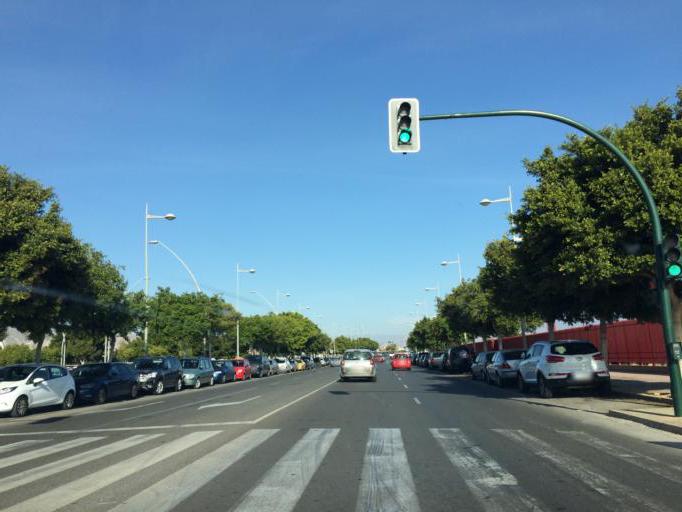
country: ES
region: Andalusia
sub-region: Provincia de Almeria
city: Almeria
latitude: 36.8380
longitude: -2.4321
